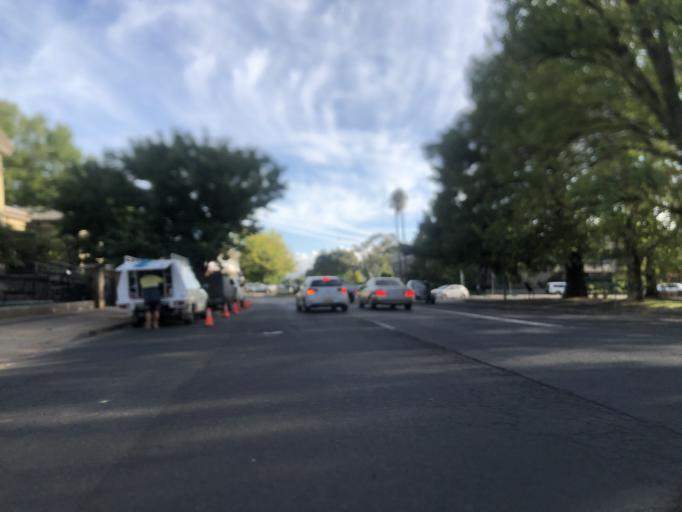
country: AU
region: New South Wales
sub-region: Orange Municipality
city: Orange
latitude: -33.2823
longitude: 149.1014
